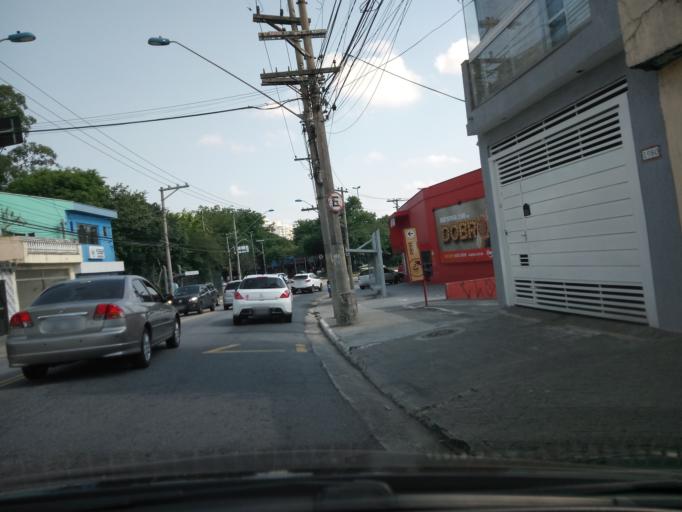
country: BR
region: Sao Paulo
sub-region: Sao Caetano Do Sul
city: Sao Caetano do Sul
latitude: -23.6463
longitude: -46.5754
